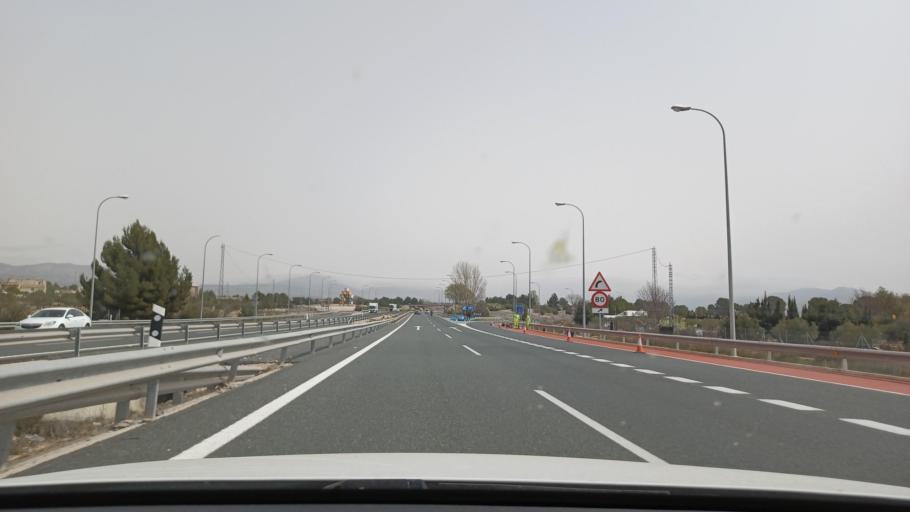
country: ES
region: Valencia
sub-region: Provincia de Alicante
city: Castalla
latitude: 38.5900
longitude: -0.6410
